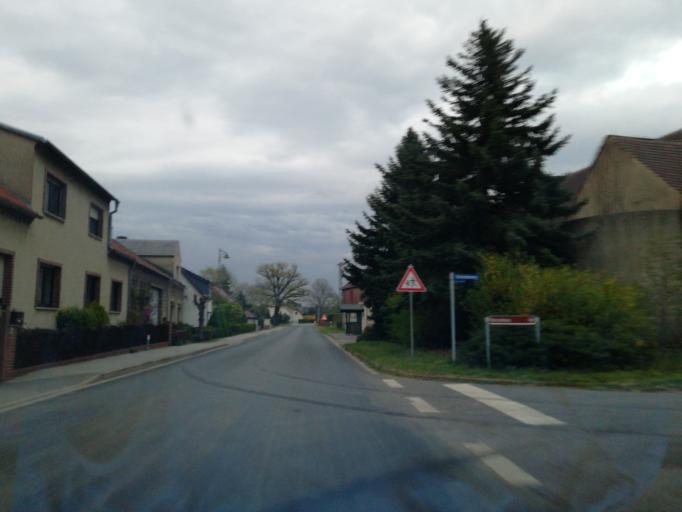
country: DE
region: Brandenburg
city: Calau
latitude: 51.7736
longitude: 13.8744
